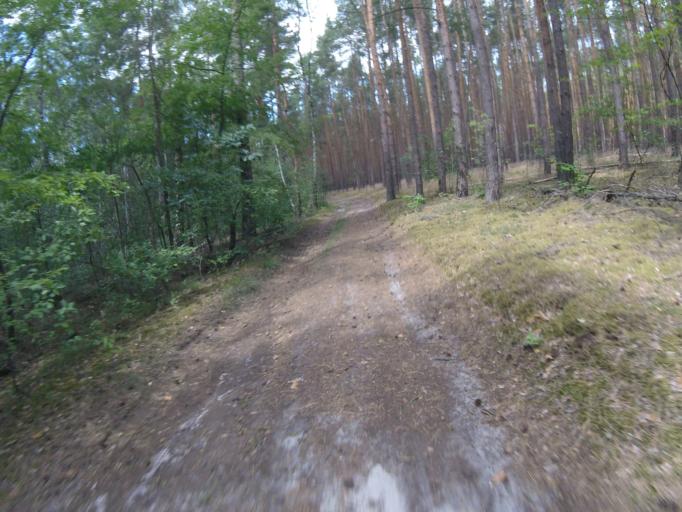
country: DE
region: Brandenburg
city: Gross Koris
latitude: 52.1986
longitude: 13.6476
